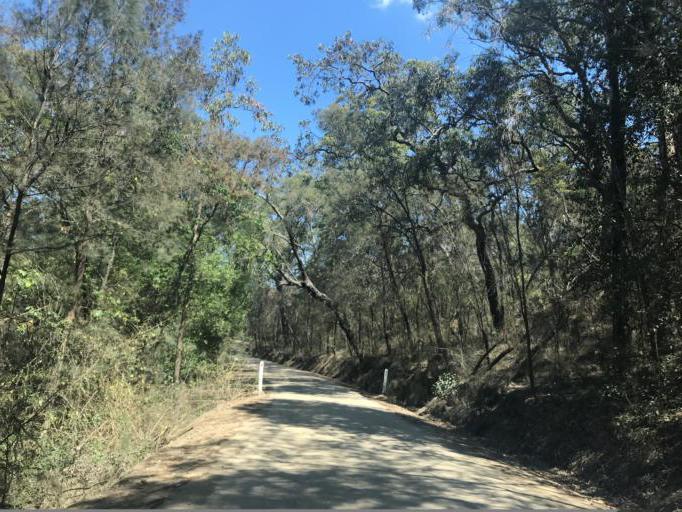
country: AU
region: New South Wales
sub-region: Hawkesbury
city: Pitt Town
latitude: -33.4069
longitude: 150.9272
